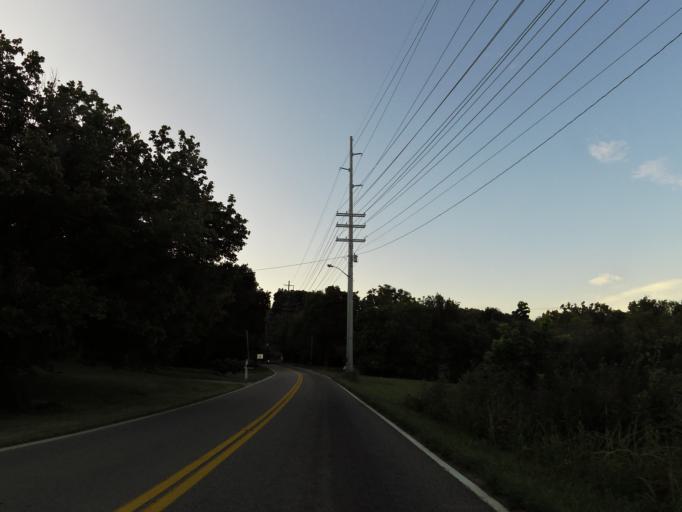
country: US
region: Tennessee
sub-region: Union County
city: Luttrell
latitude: 36.2106
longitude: -83.7456
